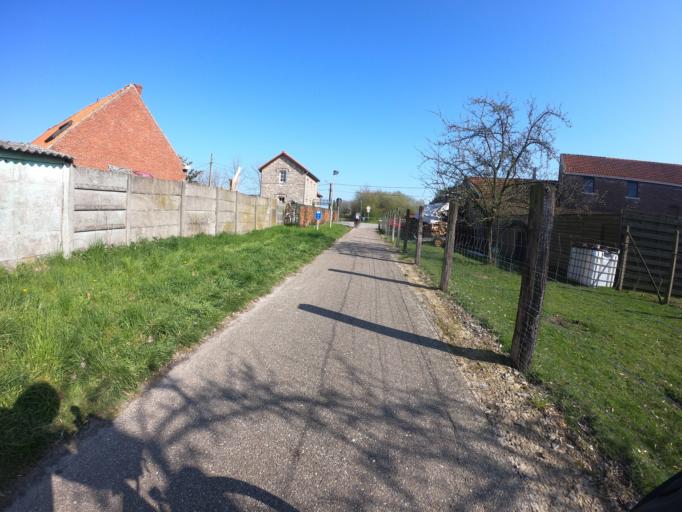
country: BE
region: Flanders
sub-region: Provincie Limburg
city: Sint-Truiden
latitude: 50.8249
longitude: 5.2128
